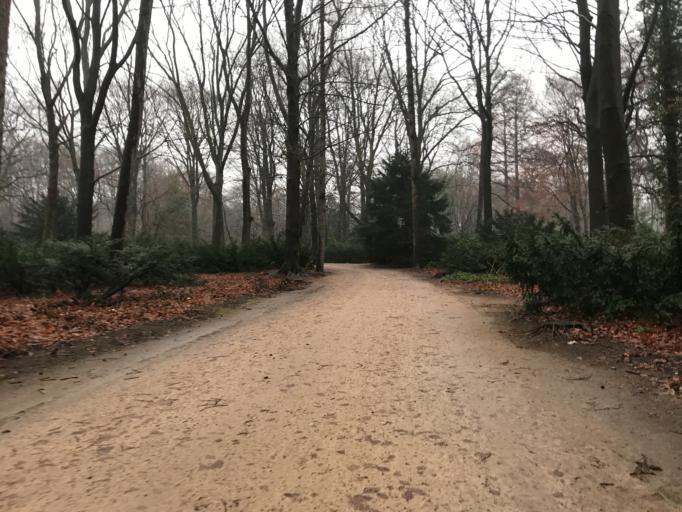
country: DE
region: Berlin
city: Hansaviertel
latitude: 52.5121
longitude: 13.3448
